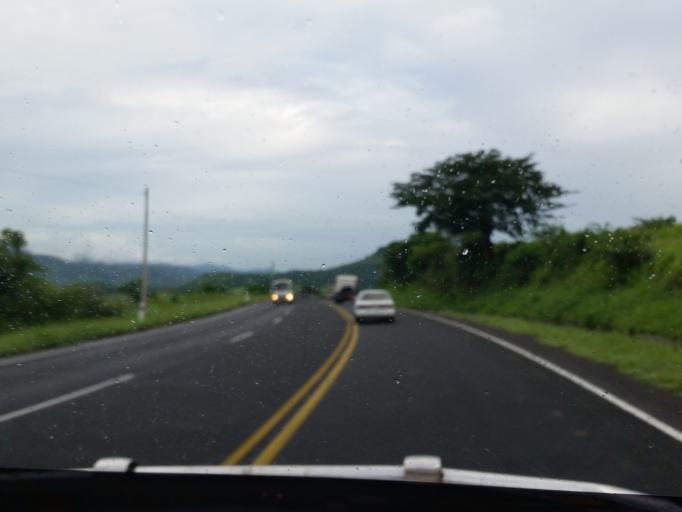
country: NI
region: Managua
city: Valle San Francisco
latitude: 12.4984
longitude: -86.0600
